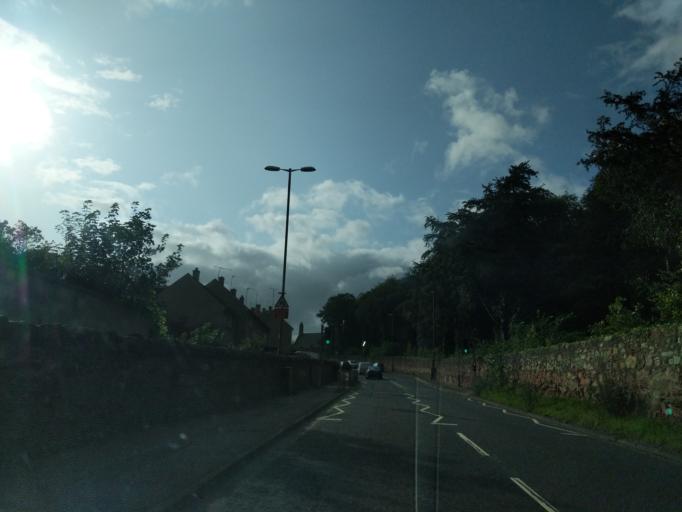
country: GB
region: Scotland
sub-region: Midlothian
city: Dalkeith
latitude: 55.8972
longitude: -3.0618
